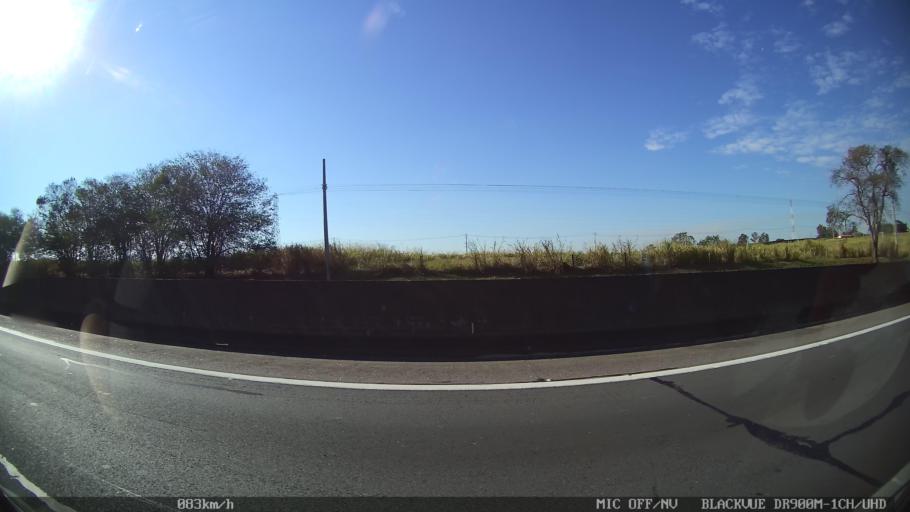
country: BR
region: Sao Paulo
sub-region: Nova Odessa
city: Nova Odessa
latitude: -22.7412
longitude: -47.2707
